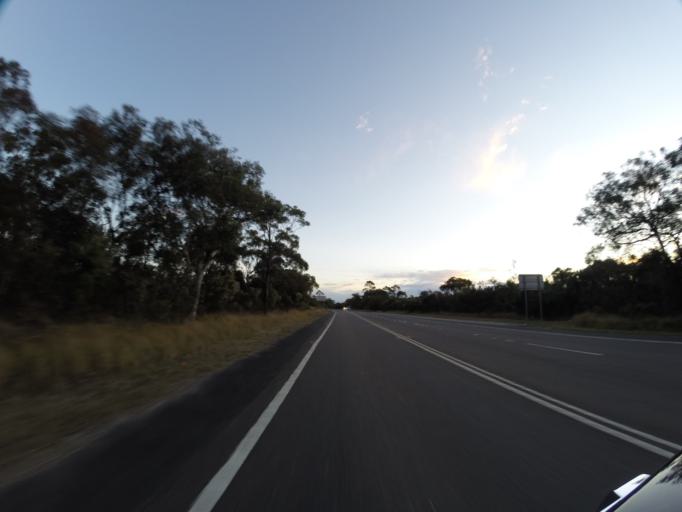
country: AU
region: New South Wales
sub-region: Liverpool
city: Holsworthy
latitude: -34.0259
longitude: 150.9683
